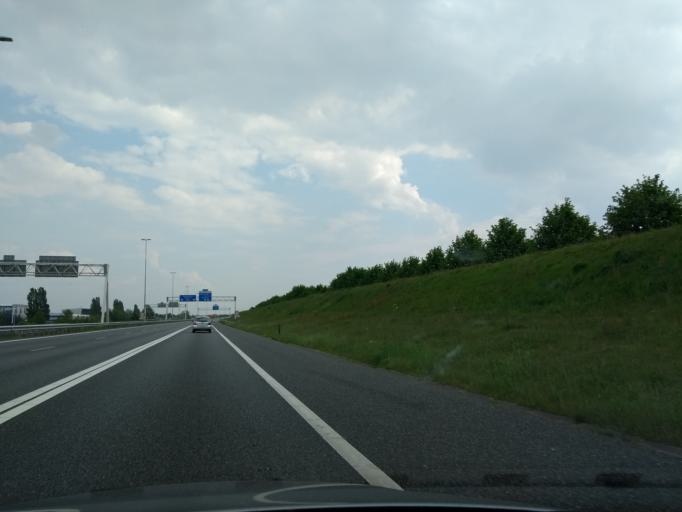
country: NL
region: Friesland
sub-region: Gemeente Heerenveen
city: Oranjewoud
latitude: 52.9569
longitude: 5.9398
